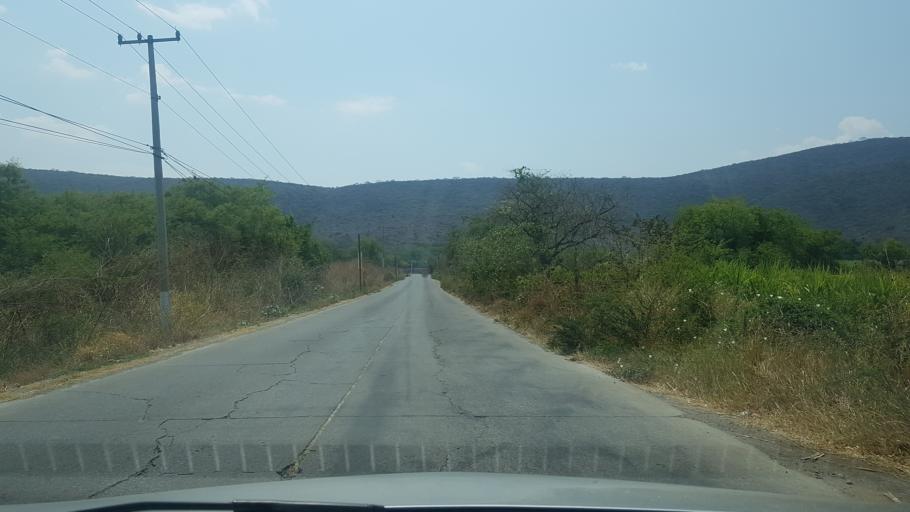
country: MX
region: Morelos
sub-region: Tlaltizapan de Zapata
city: Colonia Palo Prieto (Chipitongo)
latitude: 18.7301
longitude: -99.1211
